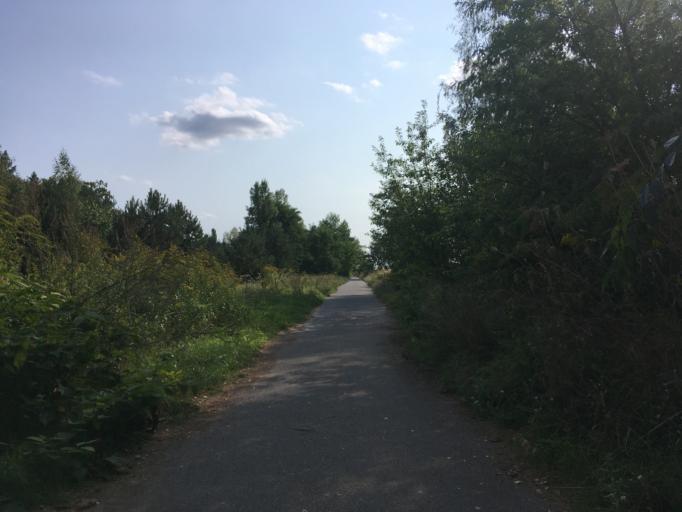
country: DE
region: Berlin
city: Frohnau
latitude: 52.6540
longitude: 13.2813
